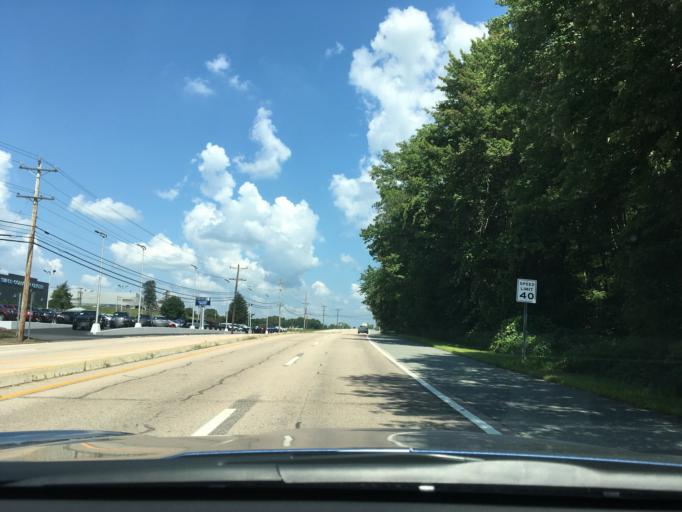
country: US
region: Rhode Island
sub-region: Kent County
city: East Greenwich
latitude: 41.6286
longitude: -71.4930
